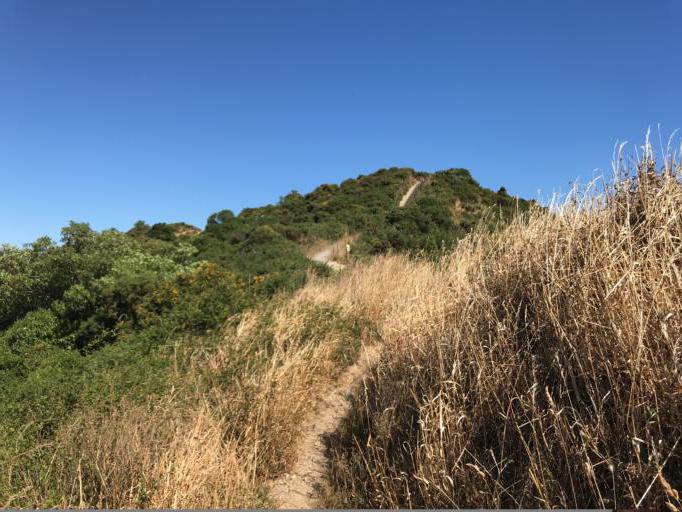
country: NZ
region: Wellington
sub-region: Wellington City
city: Brooklyn
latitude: -41.3315
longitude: 174.7664
